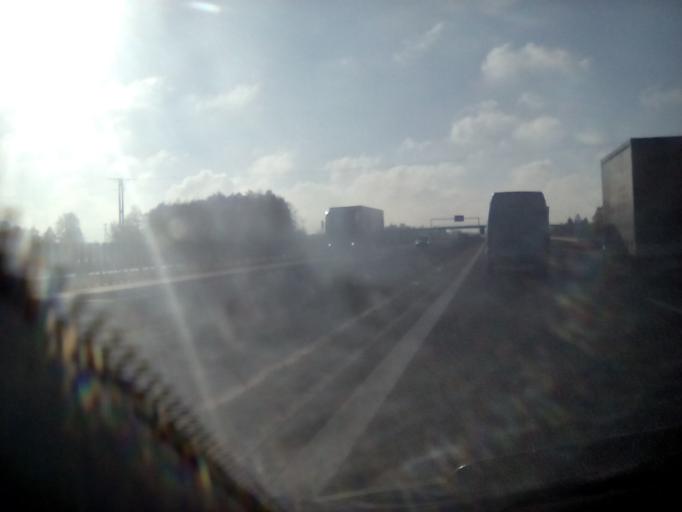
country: PL
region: Masovian Voivodeship
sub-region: Powiat grojecki
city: Grojec
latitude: 51.8176
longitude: 20.8831
